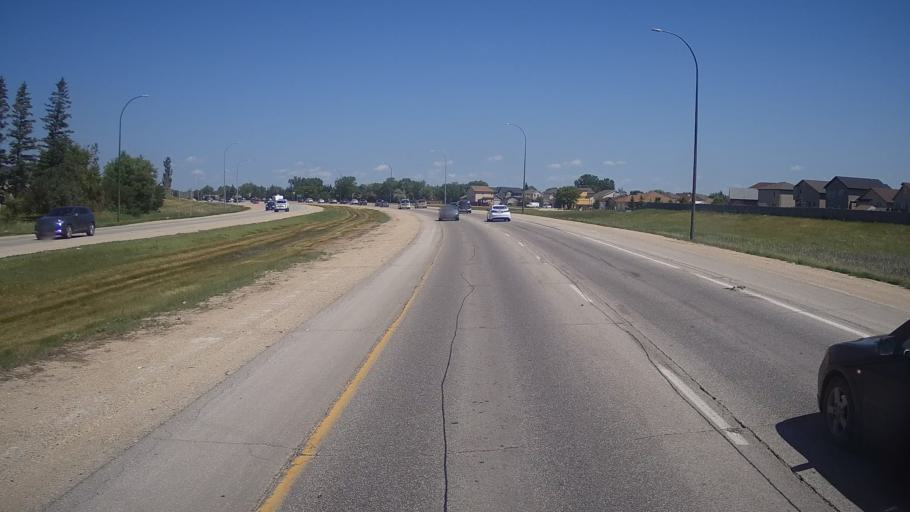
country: CA
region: Manitoba
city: Winnipeg
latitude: 49.9178
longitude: -97.0517
